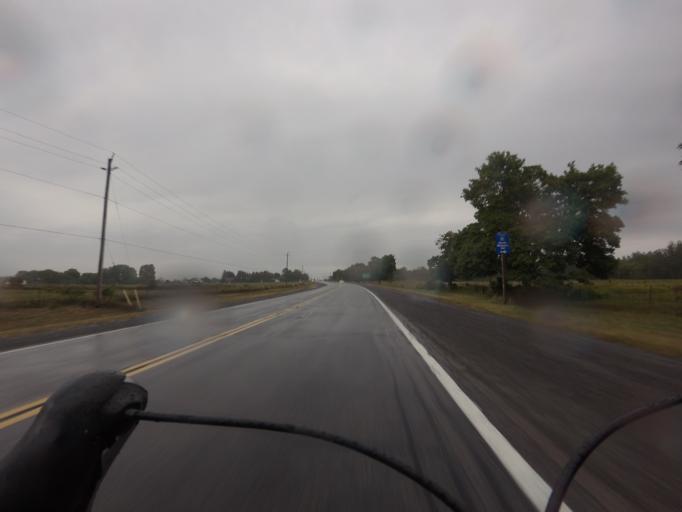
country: CA
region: Ontario
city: Bells Corners
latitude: 45.2145
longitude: -75.7145
